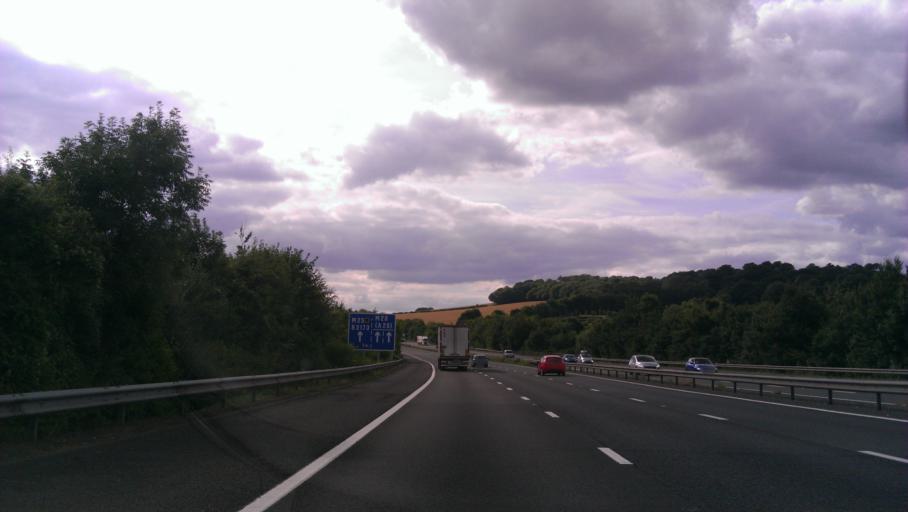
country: GB
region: England
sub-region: Kent
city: Eynsford
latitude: 51.3824
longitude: 0.2310
